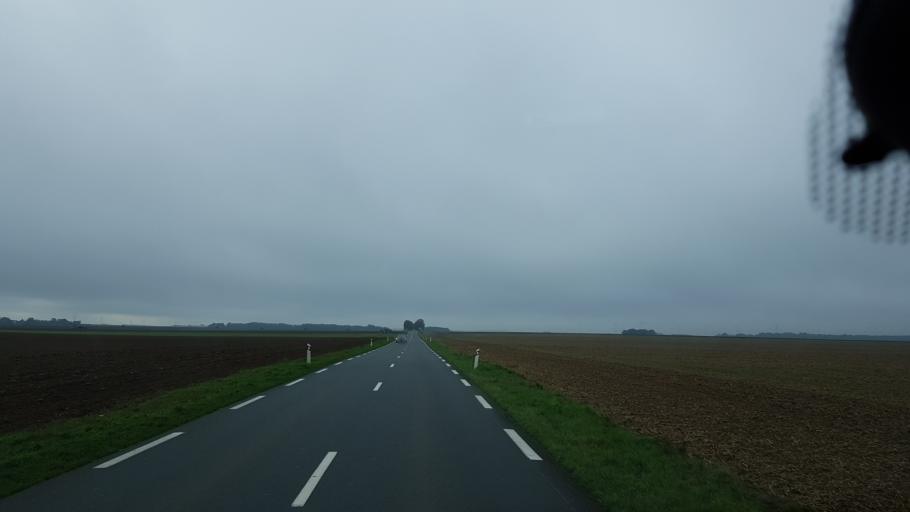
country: FR
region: Ile-de-France
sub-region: Departement de l'Essonne
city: Pussay
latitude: 48.4203
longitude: 1.9645
